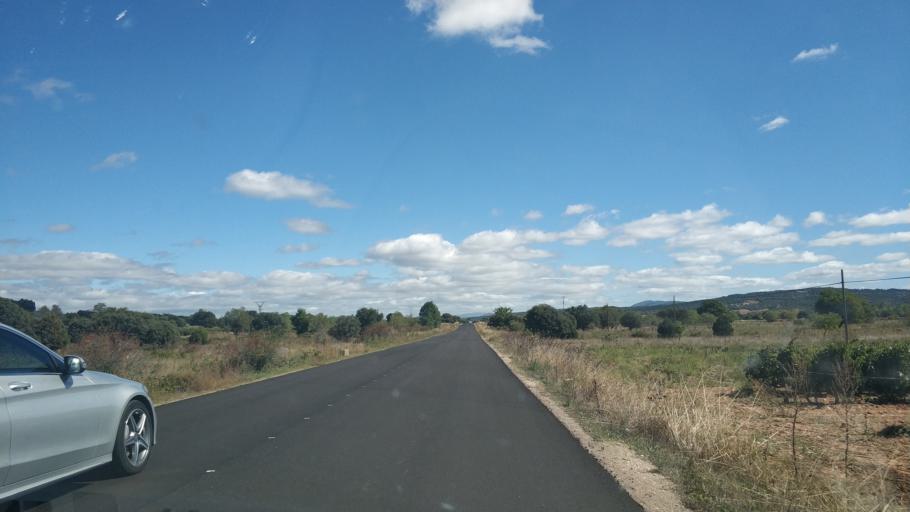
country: ES
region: Castille and Leon
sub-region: Provincia de Burgos
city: Puentedura
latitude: 42.0332
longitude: -3.6303
